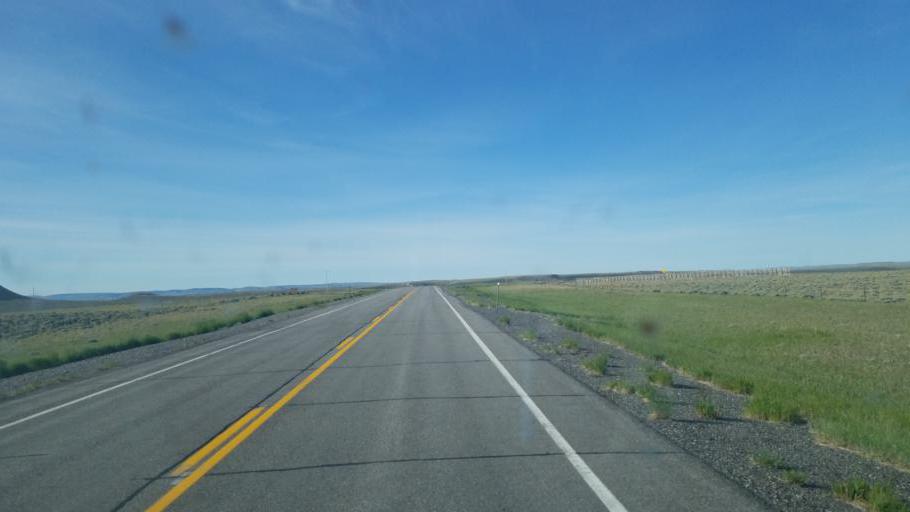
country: US
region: Wyoming
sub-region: Fremont County
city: Riverton
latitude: 42.6412
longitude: -108.1936
